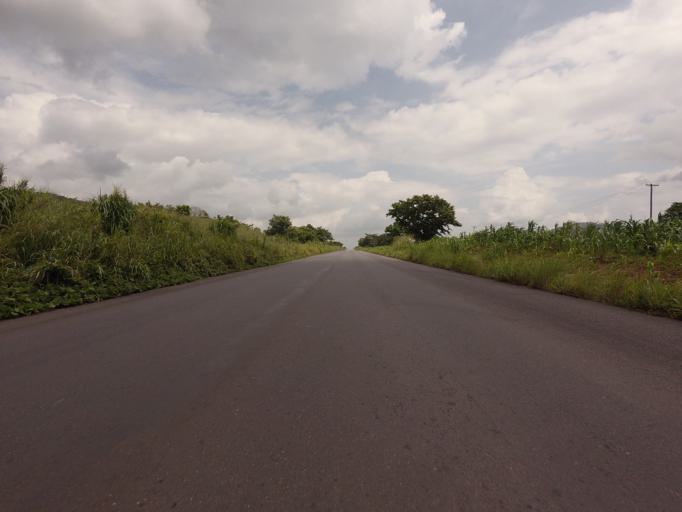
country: GH
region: Volta
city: Ho
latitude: 6.5579
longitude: 0.2615
